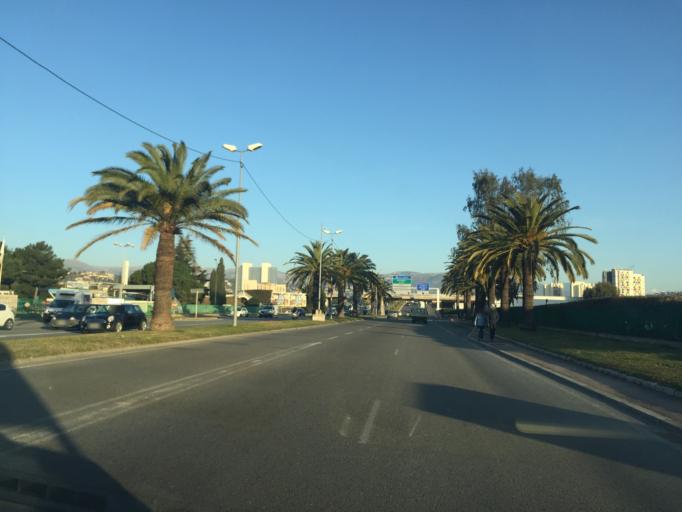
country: FR
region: Provence-Alpes-Cote d'Azur
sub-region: Departement des Alpes-Maritimes
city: Saint-Laurent-du-Var
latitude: 43.6672
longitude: 7.2050
